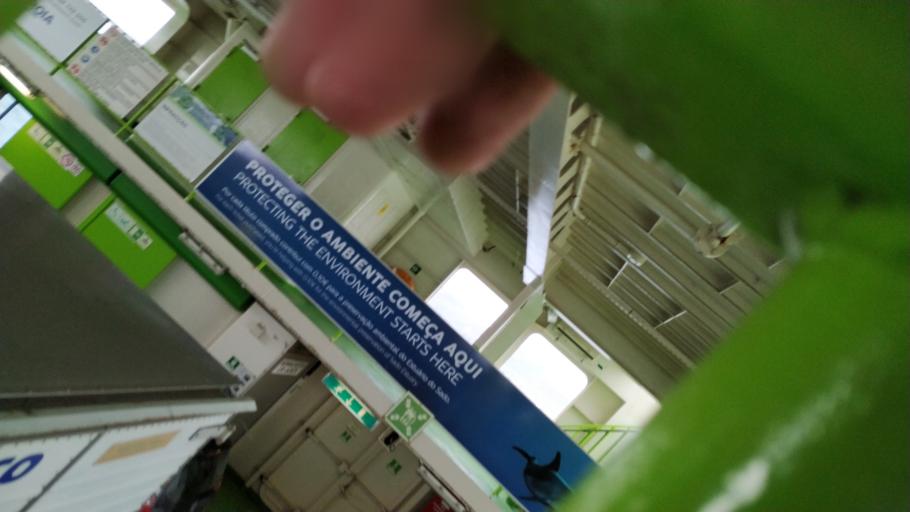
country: PT
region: Setubal
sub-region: Setubal
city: Setubal
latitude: 38.5191
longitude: -8.8856
